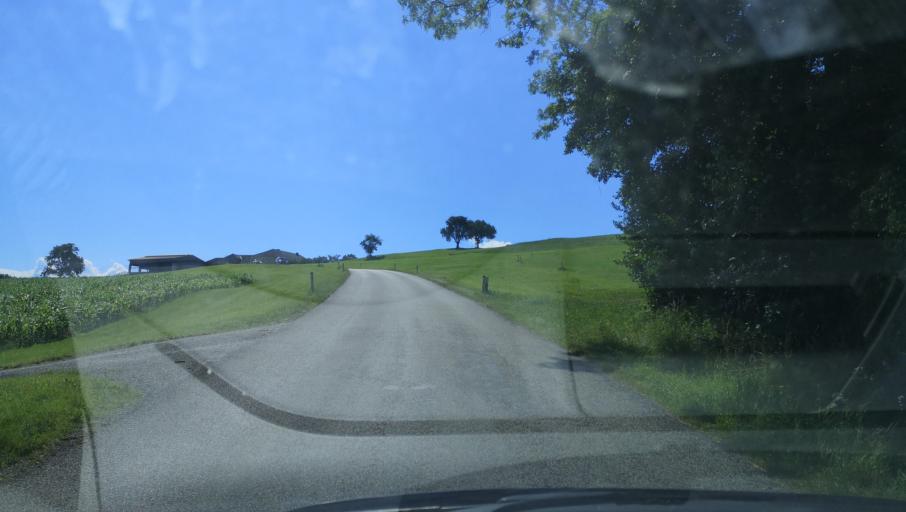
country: AT
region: Lower Austria
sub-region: Politischer Bezirk Amstetten
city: Euratsfeld
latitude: 48.0571
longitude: 14.9168
